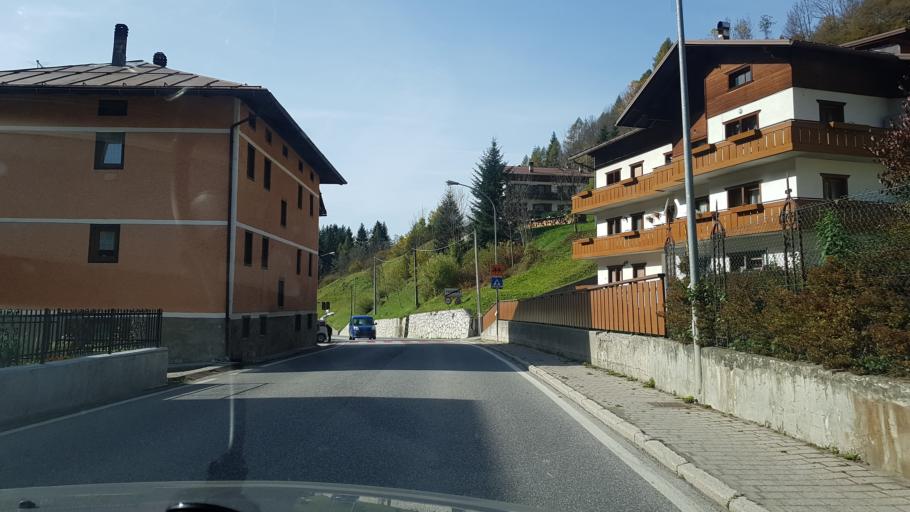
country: IT
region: Veneto
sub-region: Provincia di Belluno
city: San Pietro di Cadore
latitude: 46.5745
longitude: 12.5989
